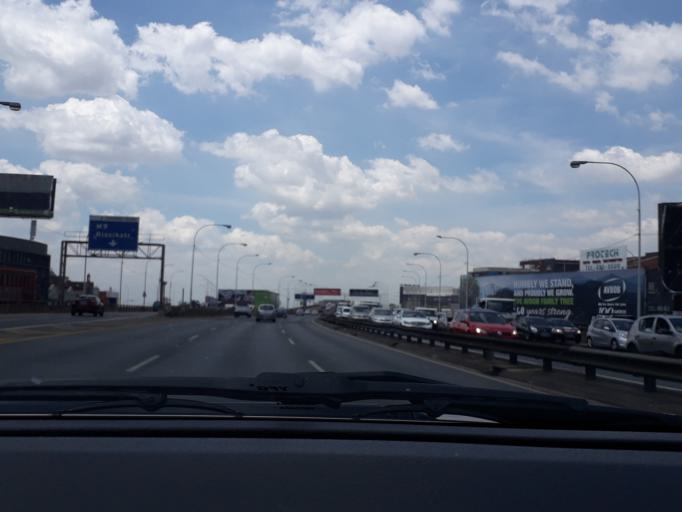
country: ZA
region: Gauteng
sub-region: City of Johannesburg Metropolitan Municipality
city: Johannesburg
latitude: -26.2120
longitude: 28.0388
